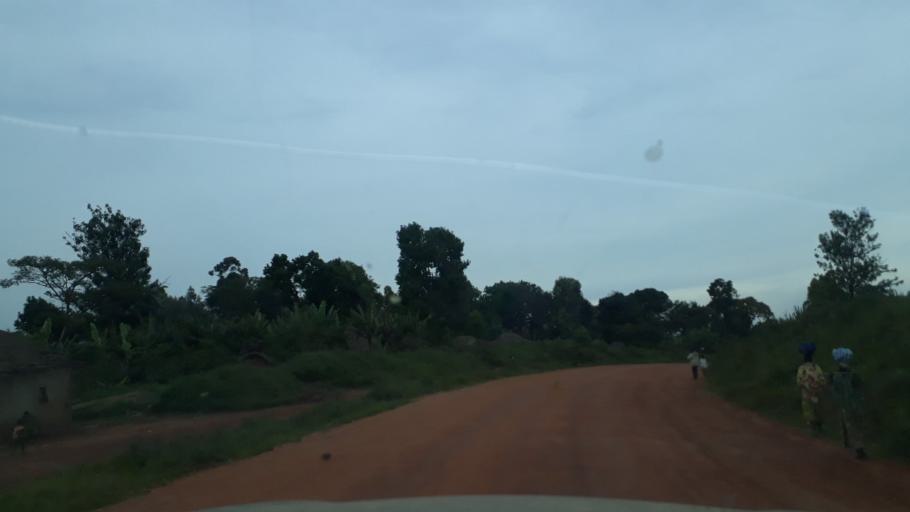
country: UG
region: Northern Region
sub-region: Zombo District
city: Paidha
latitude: 2.1696
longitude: 30.6951
